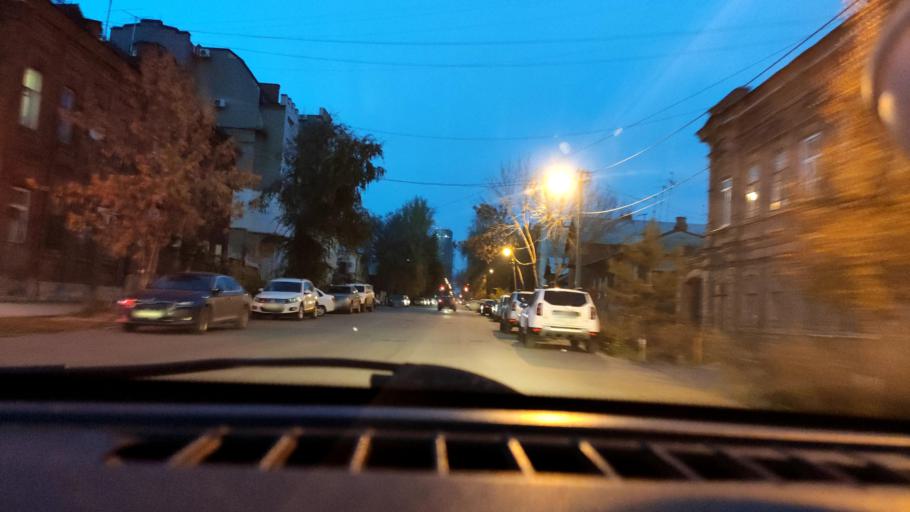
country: RU
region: Samara
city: Samara
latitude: 53.1873
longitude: 50.1040
